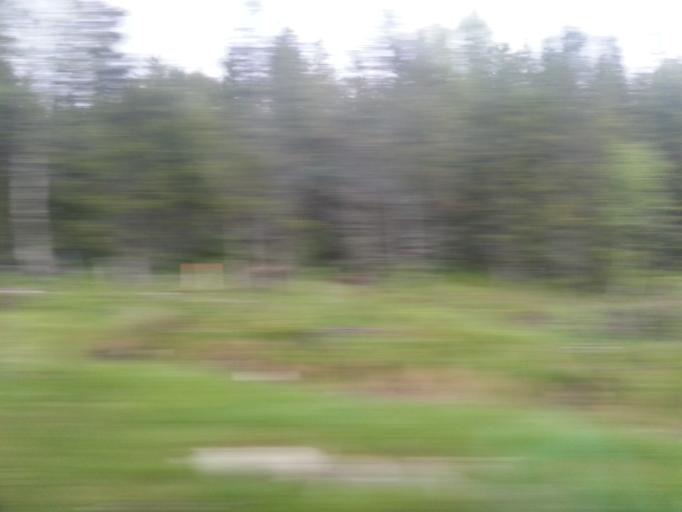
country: NO
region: Sor-Trondelag
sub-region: Rennebu
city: Berkak
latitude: 62.8564
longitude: 10.0234
